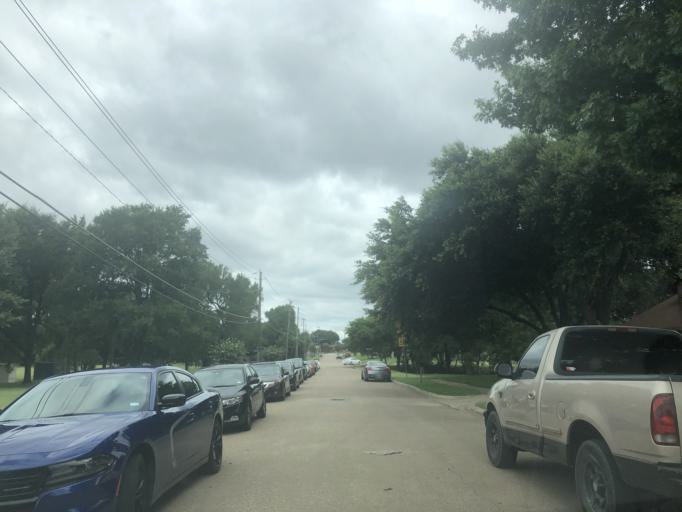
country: US
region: Texas
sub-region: Dallas County
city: Duncanville
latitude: 32.6409
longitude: -96.9437
